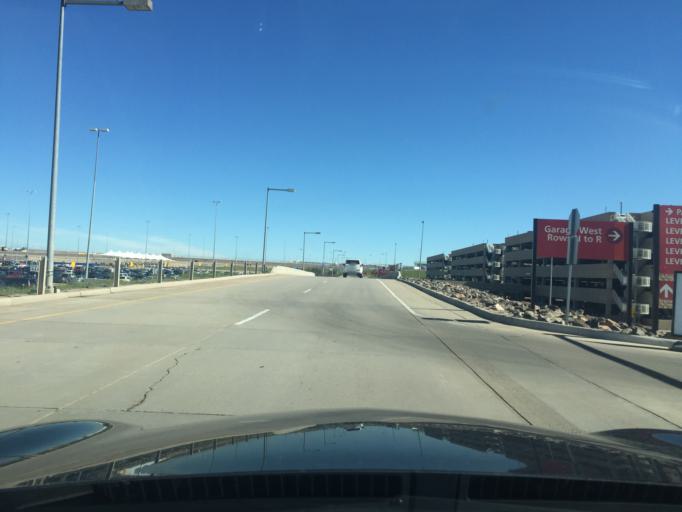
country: US
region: Colorado
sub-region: Weld County
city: Lochbuie
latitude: 39.8473
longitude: -104.6779
